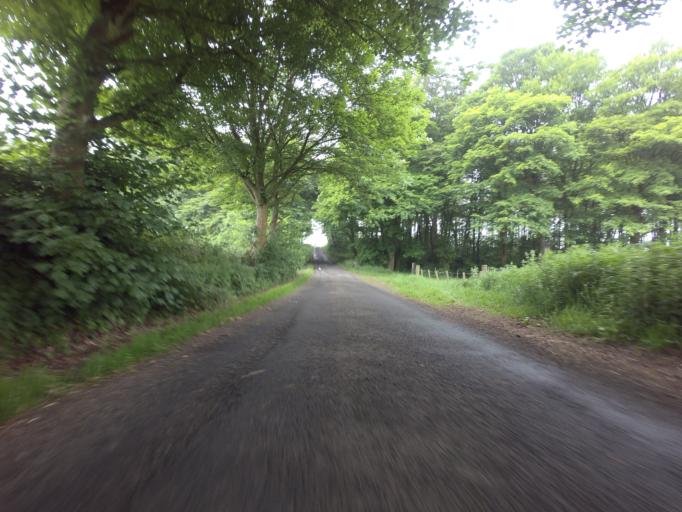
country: GB
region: Scotland
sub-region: Fife
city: Ballingry
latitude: 56.2471
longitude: -3.3379
